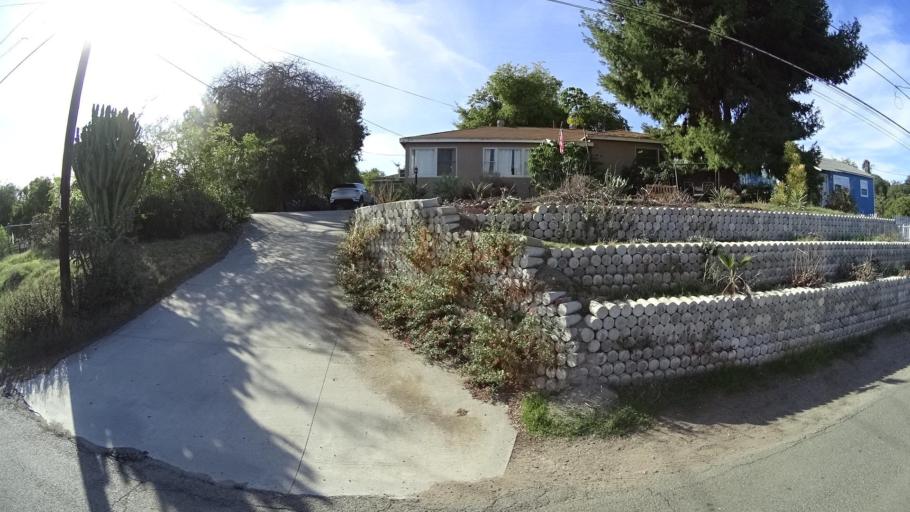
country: US
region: California
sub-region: San Diego County
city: Casa de Oro-Mount Helix
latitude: 32.7413
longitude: -116.9667
